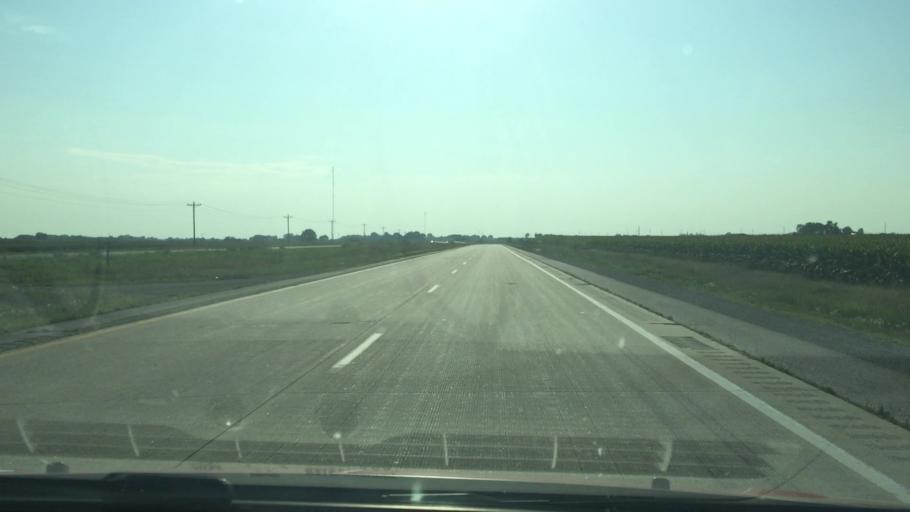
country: US
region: Iowa
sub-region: Cedar County
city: Durant
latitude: 41.5197
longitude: -90.8647
